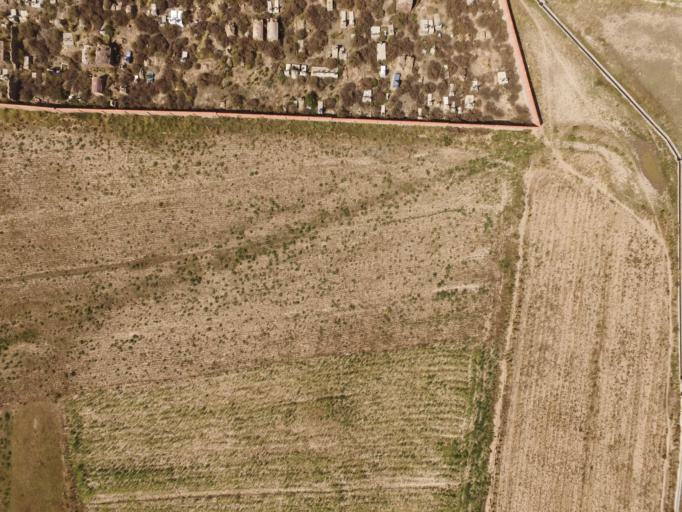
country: BO
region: Oruro
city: Challapata
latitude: -18.6925
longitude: -66.7610
